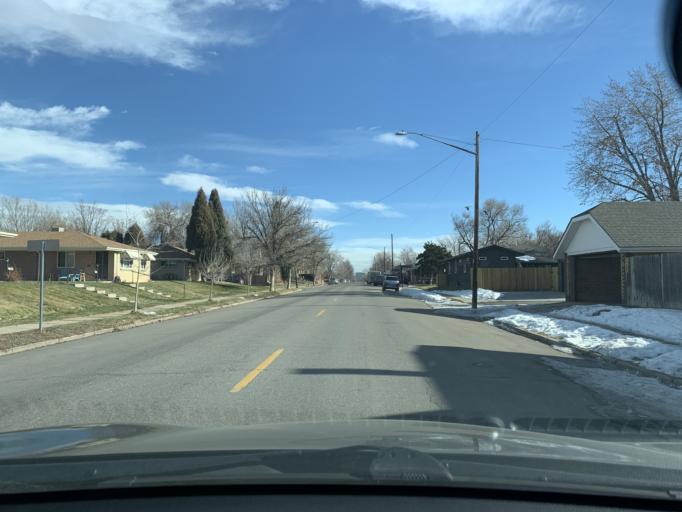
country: US
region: Colorado
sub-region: Jefferson County
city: Edgewater
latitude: 39.7512
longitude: -105.0391
